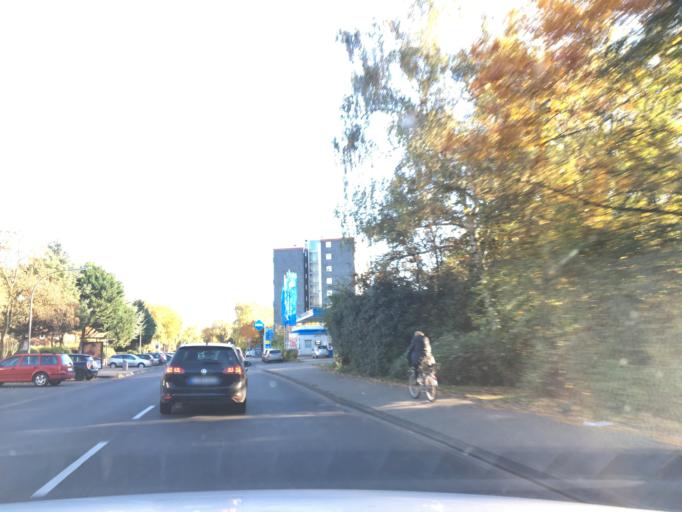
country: DE
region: North Rhine-Westphalia
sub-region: Regierungsbezirk Koln
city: Bilderstoeckchen
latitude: 50.9700
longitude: 6.9266
